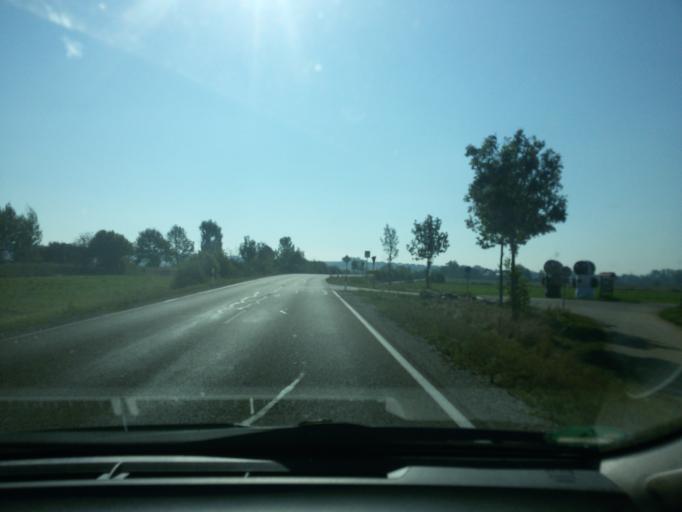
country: DE
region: Bavaria
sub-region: Swabia
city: Auhausen
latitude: 49.0225
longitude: 10.6165
